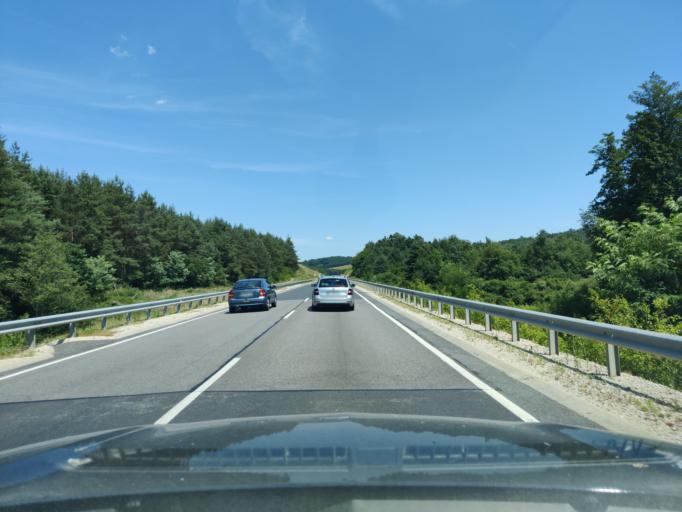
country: HU
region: Zala
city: Zalalovo
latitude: 46.8310
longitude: 16.6068
